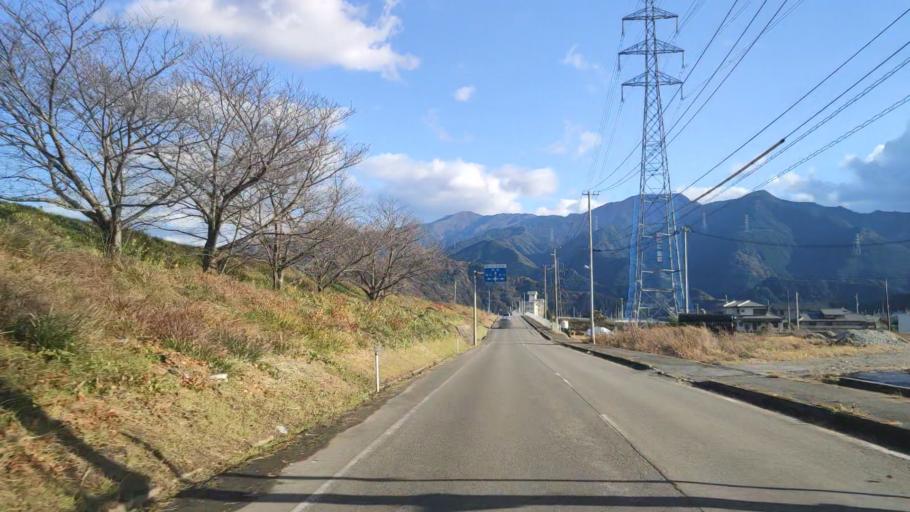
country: JP
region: Ehime
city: Saijo
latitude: 33.9049
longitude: 133.1791
